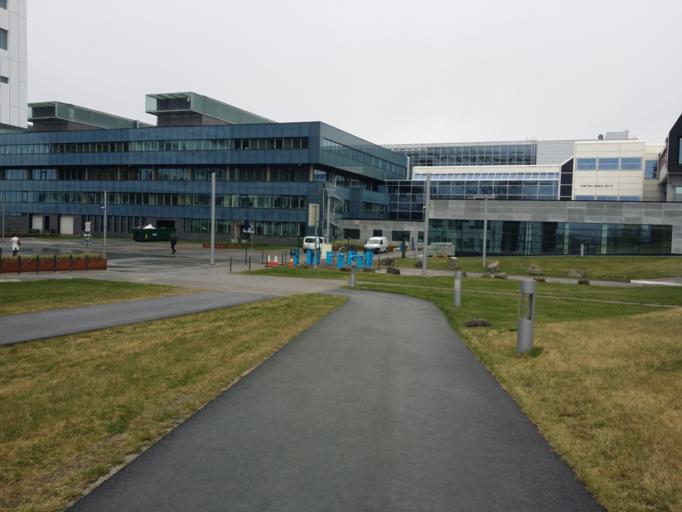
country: NO
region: Akershus
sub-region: Baerum
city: Lysaker
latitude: 59.8965
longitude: 10.6286
